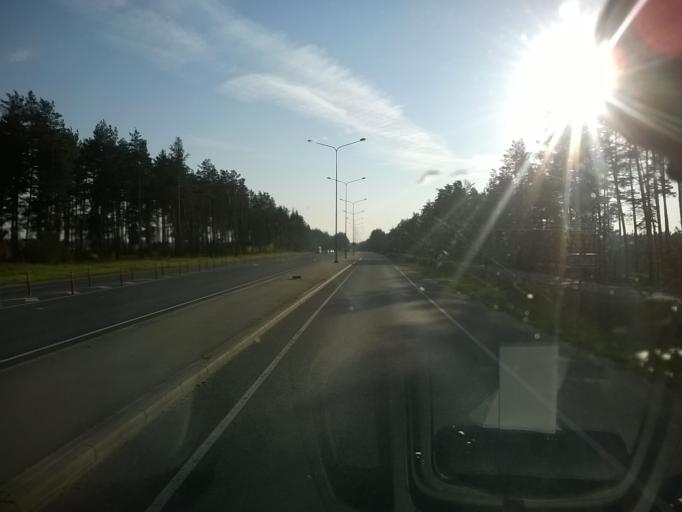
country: EE
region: Harju
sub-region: Saku vald
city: Saku
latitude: 59.3353
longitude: 24.6981
